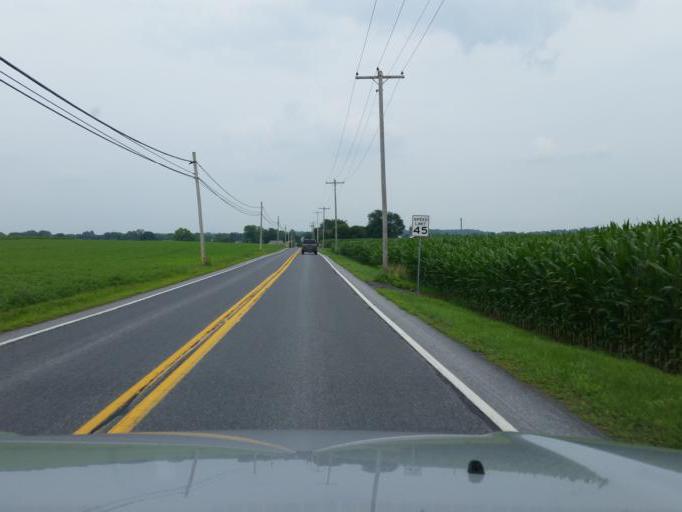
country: US
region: Pennsylvania
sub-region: Lancaster County
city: Lititz
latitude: 40.1553
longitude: -76.3421
